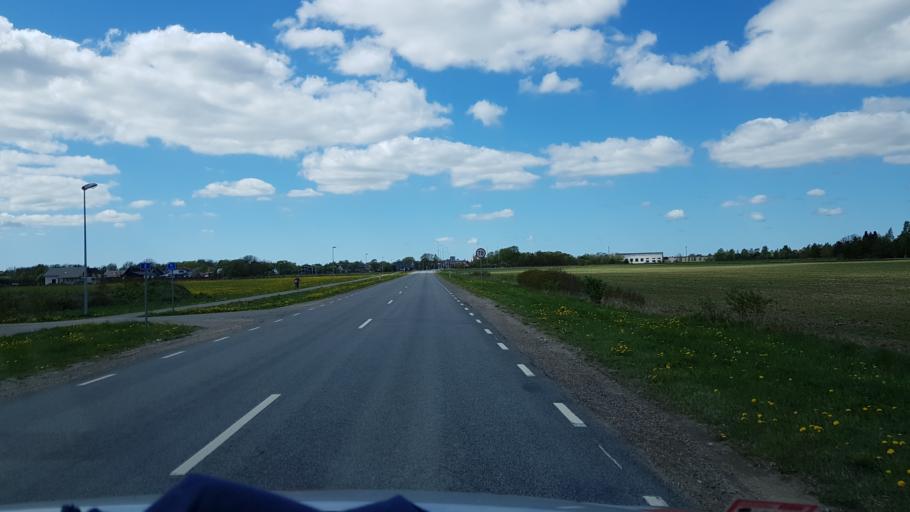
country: EE
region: Saare
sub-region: Kuressaare linn
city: Kuressaare
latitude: 58.2552
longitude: 22.5257
